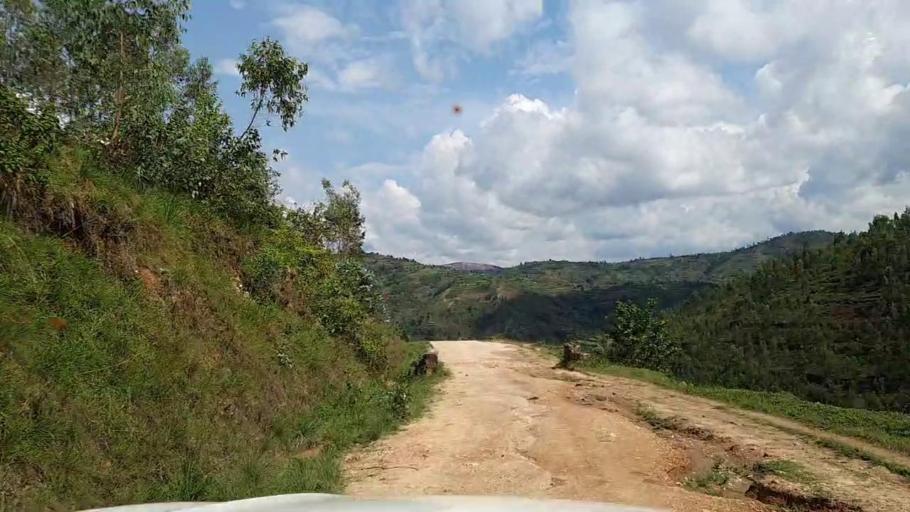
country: RW
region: Southern Province
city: Gikongoro
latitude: -2.3975
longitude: 29.5574
